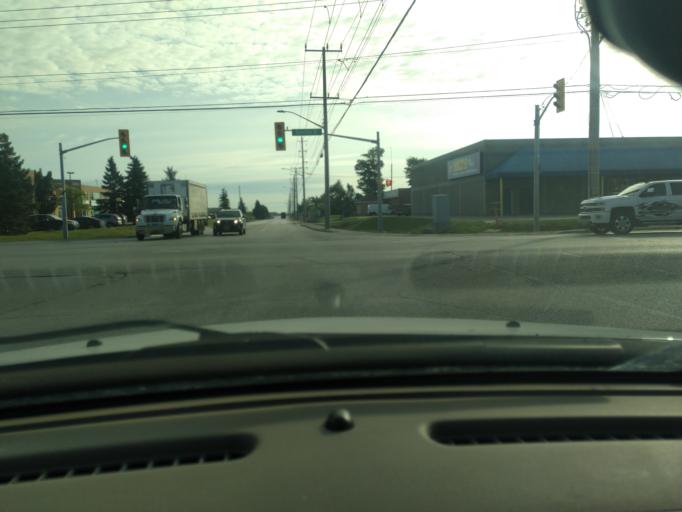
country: CA
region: Ontario
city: Innisfil
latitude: 44.3321
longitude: -79.6778
